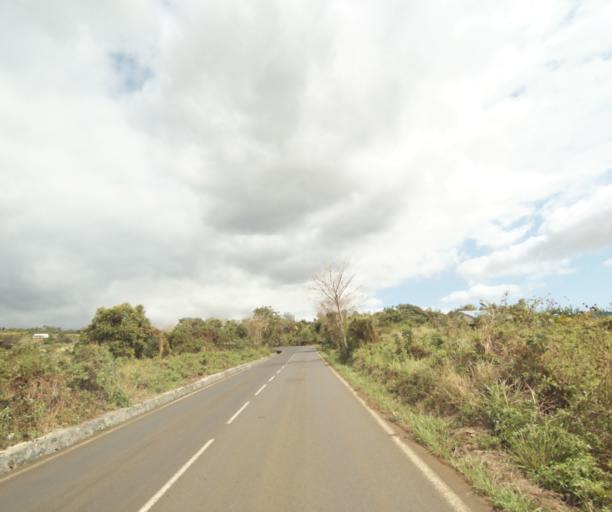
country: RE
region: Reunion
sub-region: Reunion
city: Saint-Paul
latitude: -21.0336
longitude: 55.2866
